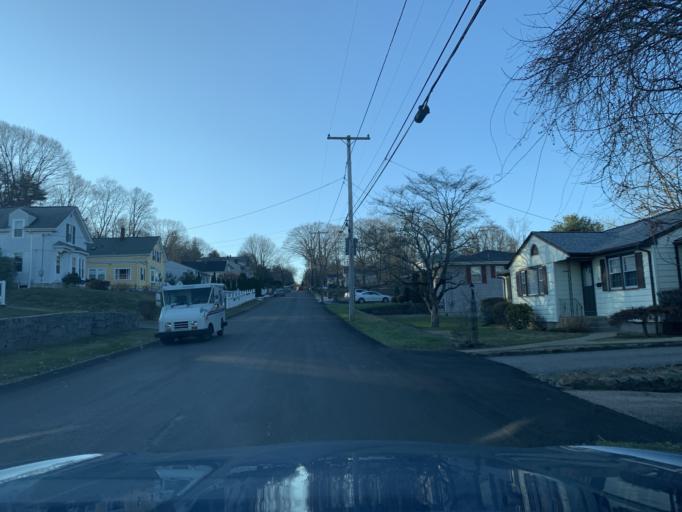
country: US
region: Rhode Island
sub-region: Kent County
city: West Warwick
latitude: 41.7123
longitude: -71.5274
